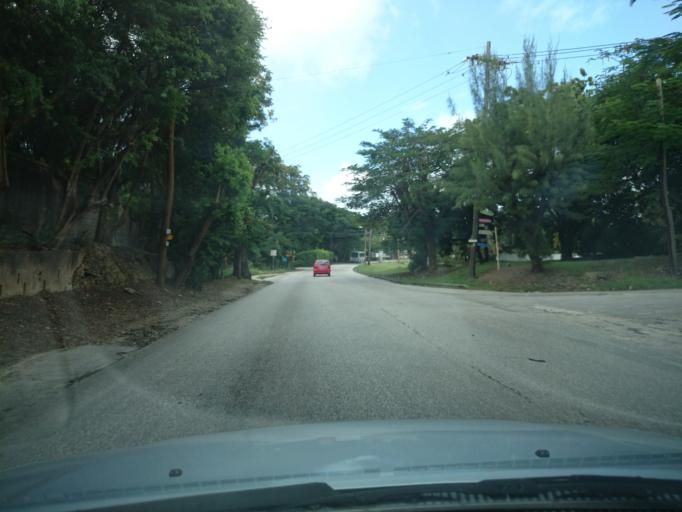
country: BB
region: Saint James
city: Holetown
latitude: 13.1761
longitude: -59.6368
